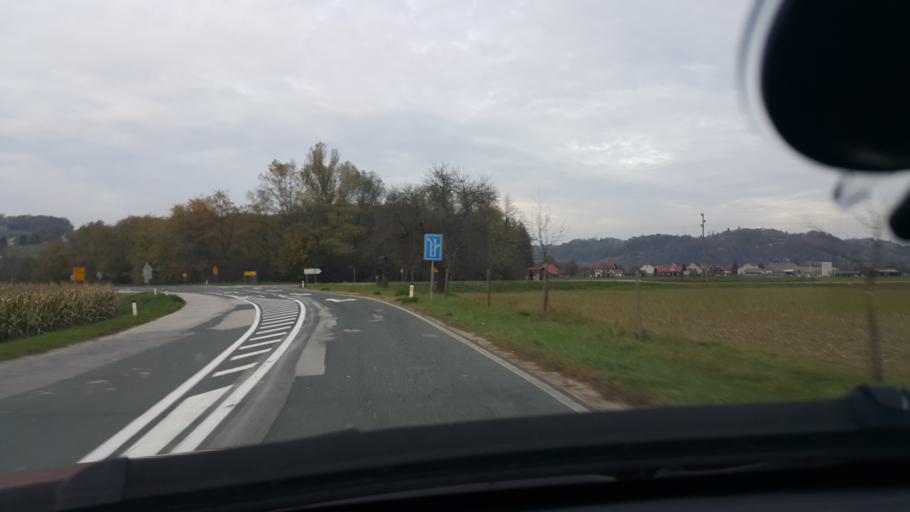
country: SI
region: Bistrica ob Sotli
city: Bistrica ob Sotli
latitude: 46.0612
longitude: 15.6565
